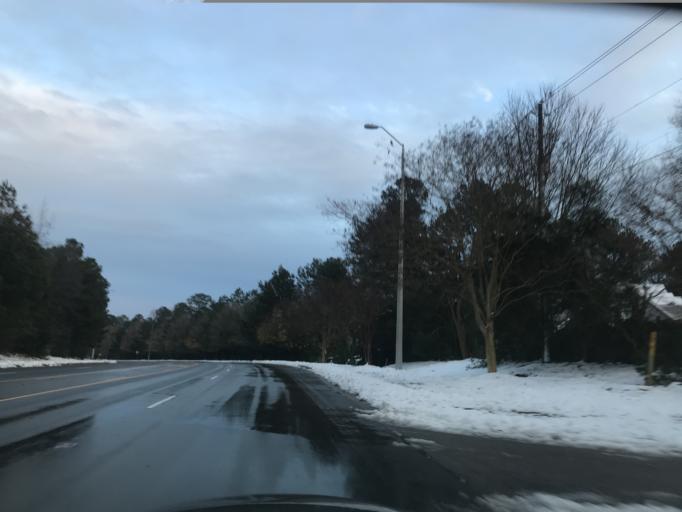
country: US
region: North Carolina
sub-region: Wake County
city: Wake Forest
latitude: 35.8992
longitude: -78.5755
